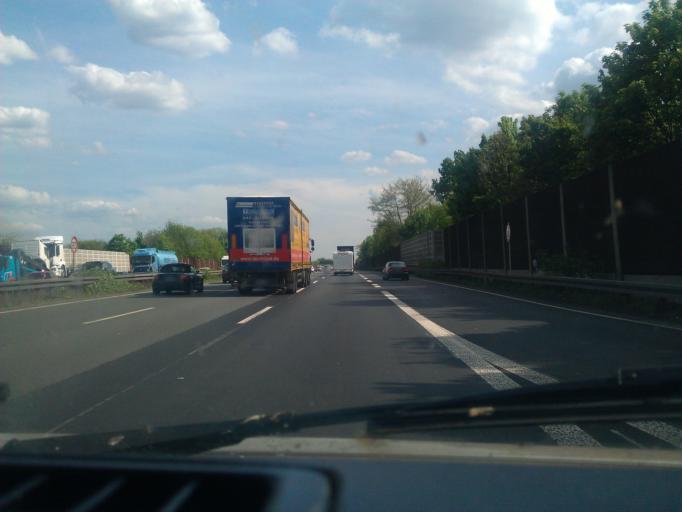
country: DE
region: North Rhine-Westphalia
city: Meiderich
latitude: 51.5139
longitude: 6.8171
